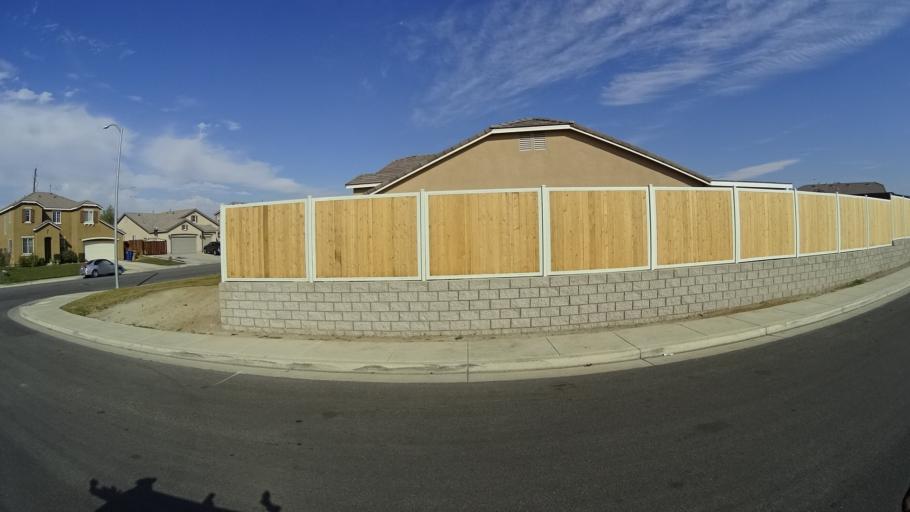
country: US
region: California
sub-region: Kern County
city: Bakersfield
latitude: 35.3934
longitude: -118.8838
